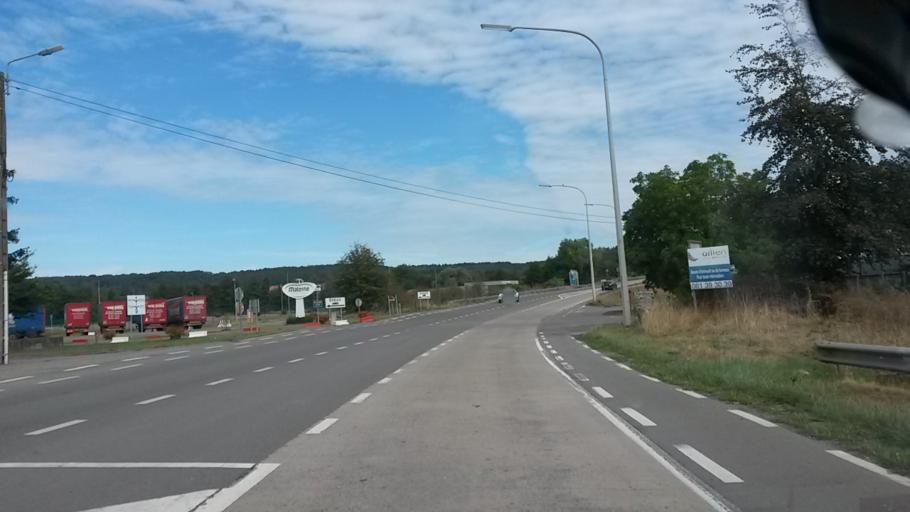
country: BE
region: Wallonia
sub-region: Province de Namur
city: Floreffe
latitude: 50.4473
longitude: 4.7677
